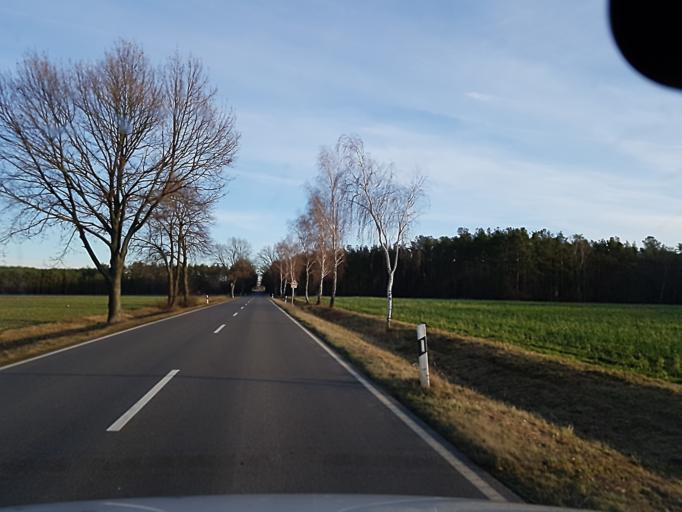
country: DE
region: Brandenburg
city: Finsterwalde
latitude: 51.6181
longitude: 13.7430
